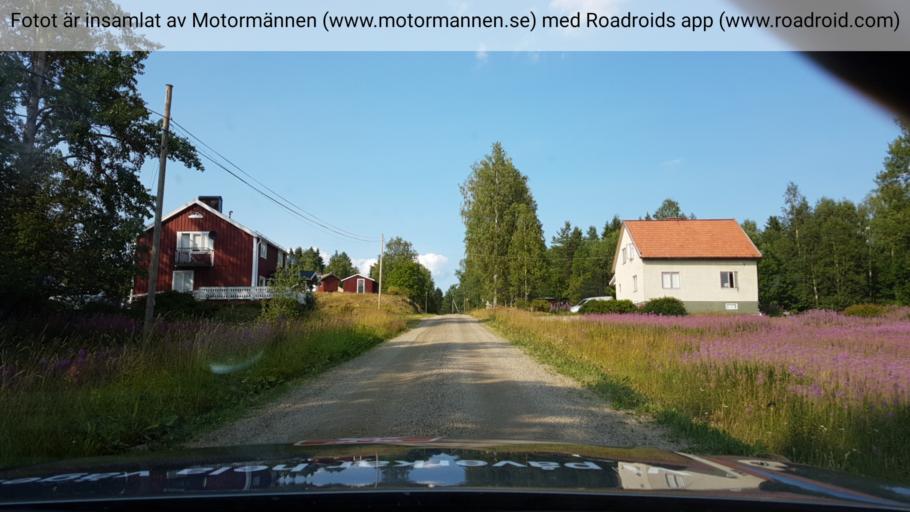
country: SE
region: Jaemtland
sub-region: OEstersunds Kommun
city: Brunflo
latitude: 62.6117
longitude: 14.9442
